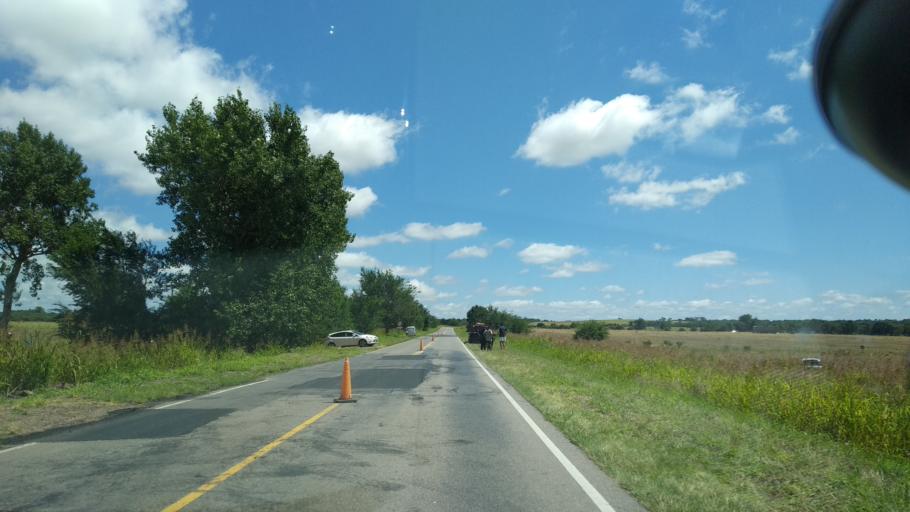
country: AR
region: Cordoba
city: Villa Cura Brochero
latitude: -31.6204
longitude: -65.1092
